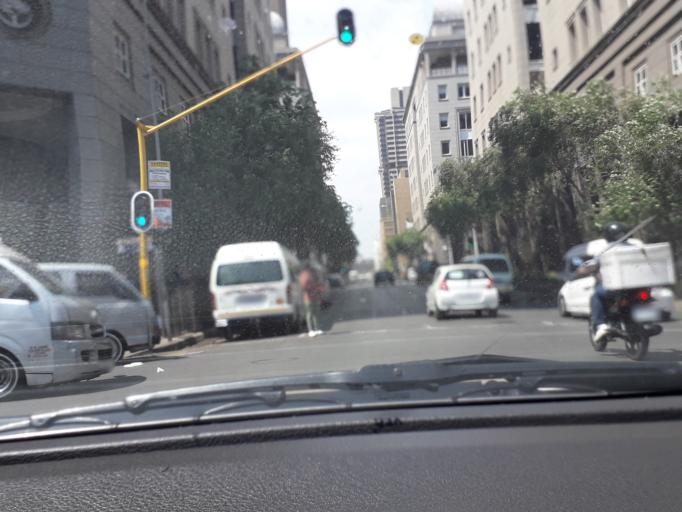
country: ZA
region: Gauteng
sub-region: City of Johannesburg Metropolitan Municipality
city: Johannesburg
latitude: -26.2019
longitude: 28.0392
